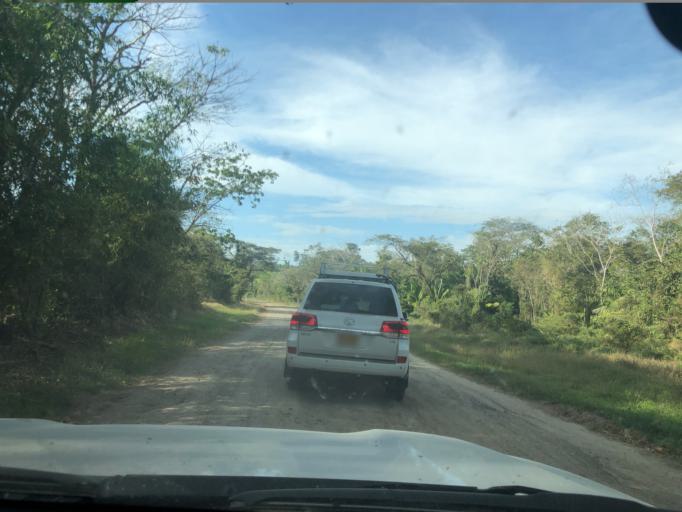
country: CR
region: Alajuela
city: San Jose
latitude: 11.1143
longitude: -85.2827
